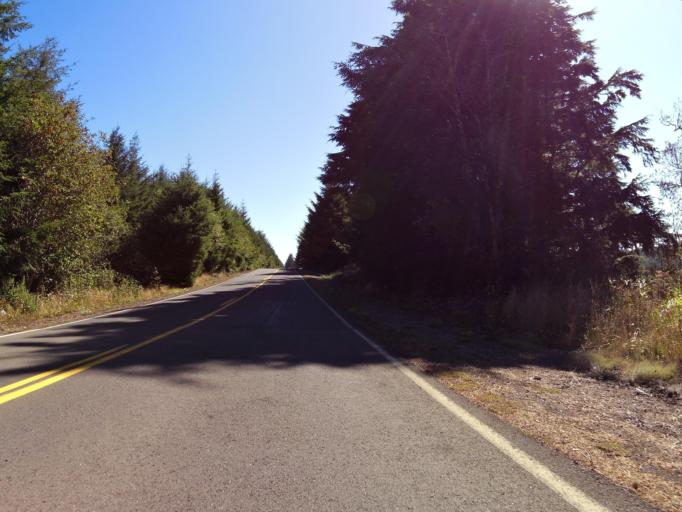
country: US
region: Oregon
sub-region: Coos County
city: Barview
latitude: 43.2667
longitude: -124.3456
